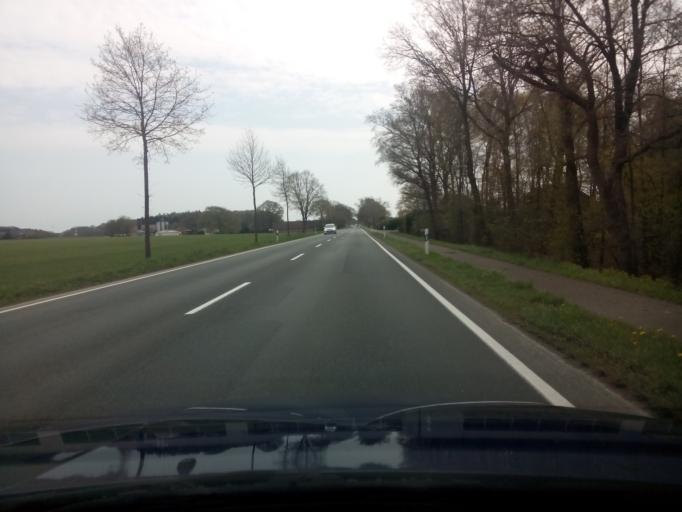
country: DE
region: Lower Saxony
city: Sustedt
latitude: 52.8528
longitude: 8.8918
